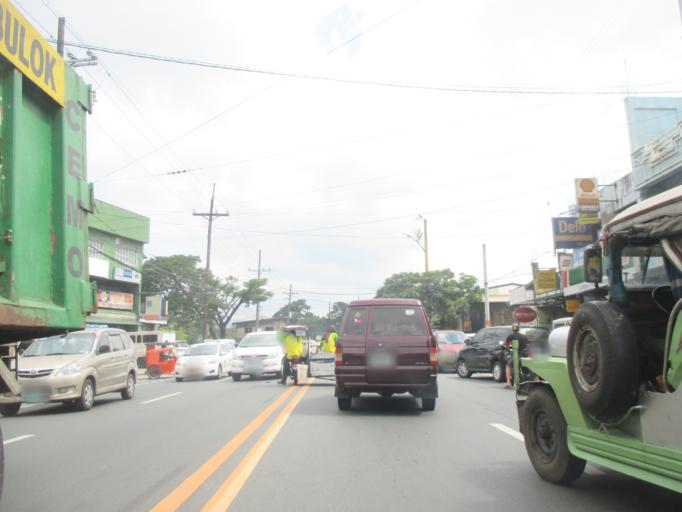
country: PH
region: Calabarzon
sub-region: Province of Rizal
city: Antipolo
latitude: 14.6508
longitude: 121.1080
